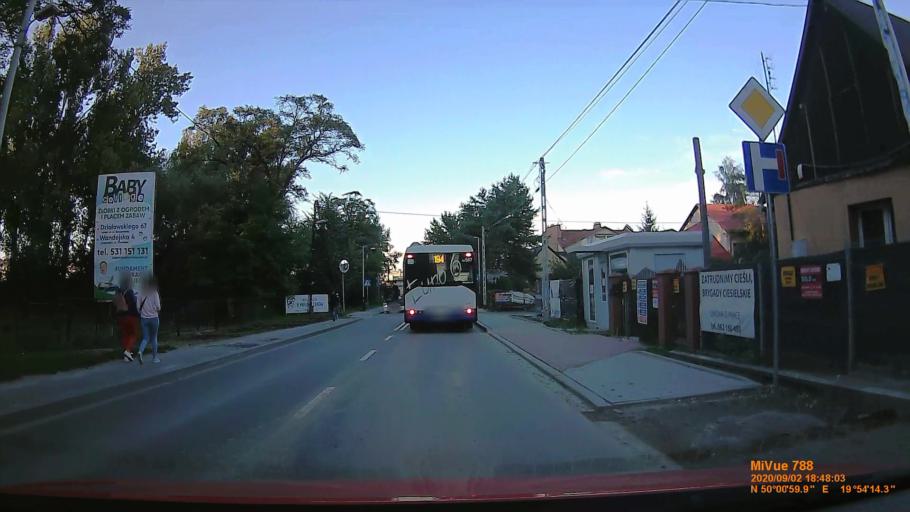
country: PL
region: Lesser Poland Voivodeship
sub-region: Krakow
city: Sidzina
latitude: 50.0168
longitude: 19.9041
